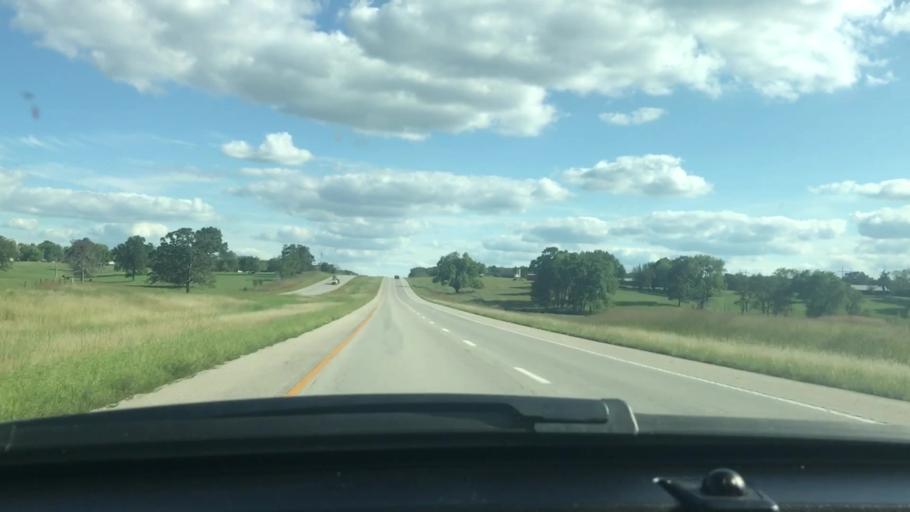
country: US
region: Missouri
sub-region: Howell County
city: West Plains
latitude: 36.8405
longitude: -91.9183
